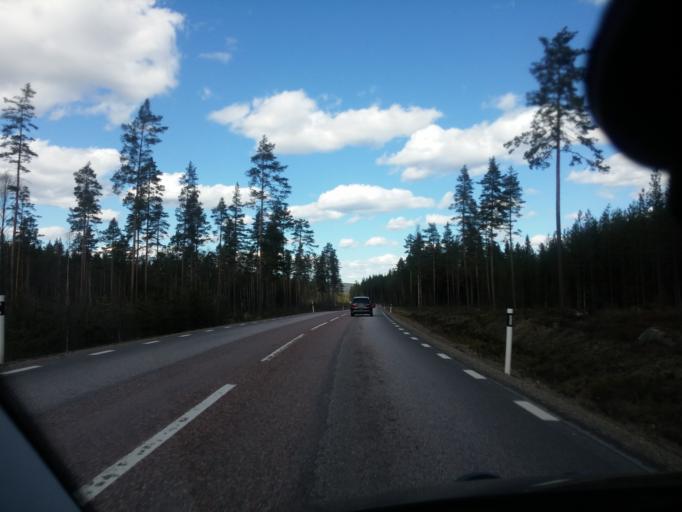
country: SE
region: Dalarna
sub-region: Faluns Kommun
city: Svardsjo
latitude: 60.7764
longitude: 15.7533
